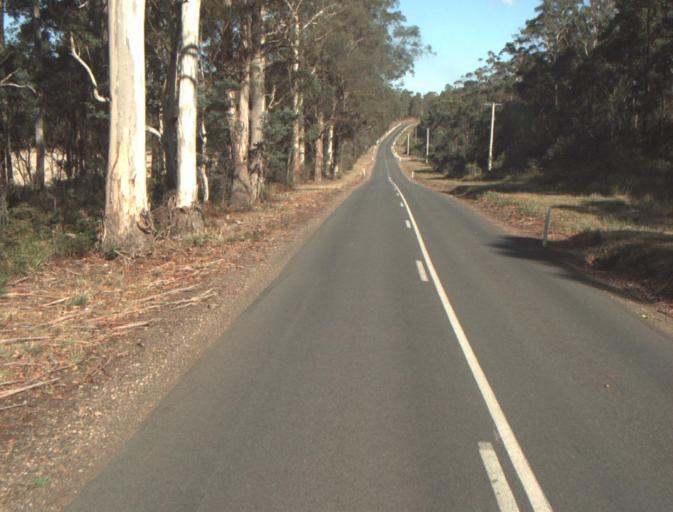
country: AU
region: Tasmania
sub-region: Launceston
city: Mayfield
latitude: -41.2942
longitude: 147.1316
